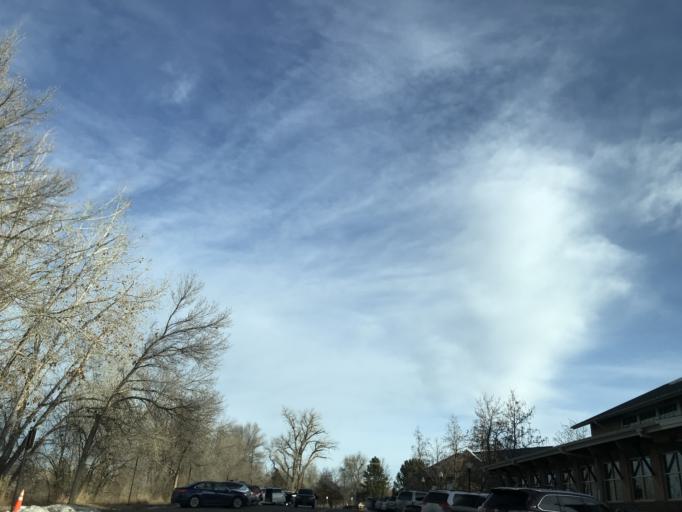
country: US
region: Colorado
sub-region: Arapahoe County
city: Littleton
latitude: 39.6140
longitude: -105.0129
